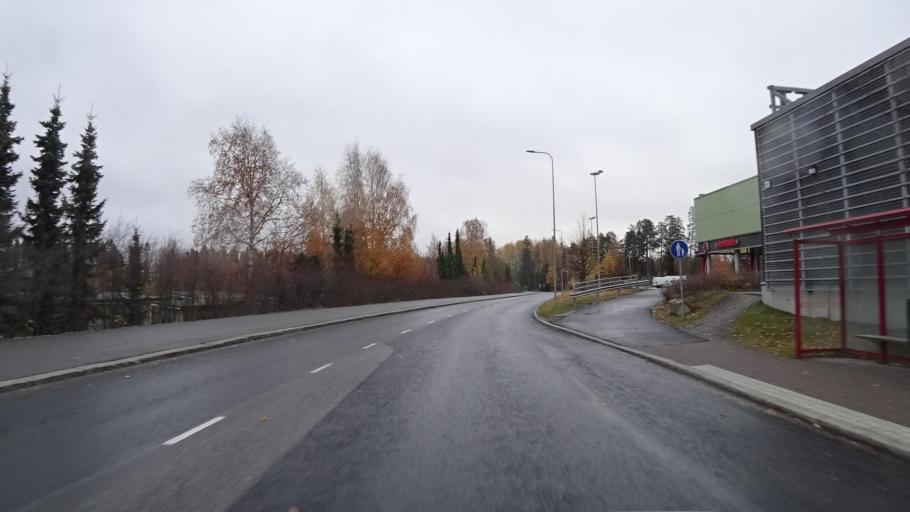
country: FI
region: Northern Savo
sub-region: Kuopio
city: Kuopio
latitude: 62.9329
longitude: 27.6759
